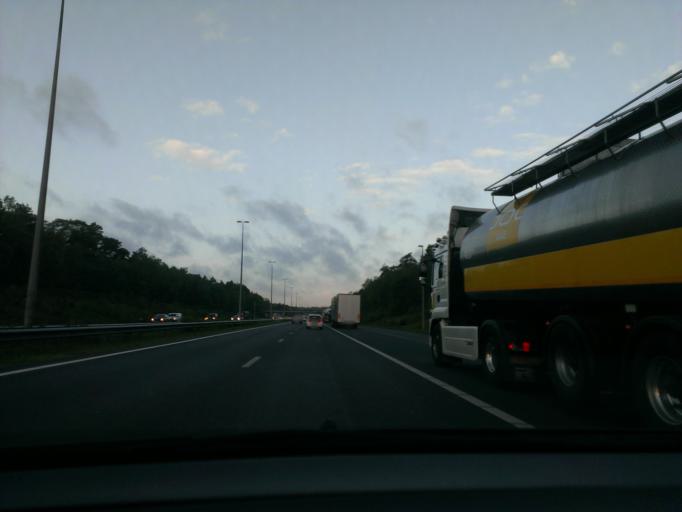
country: NL
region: Gelderland
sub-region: Gemeente Apeldoorn
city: Beekbergen
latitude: 52.1324
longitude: 5.9747
